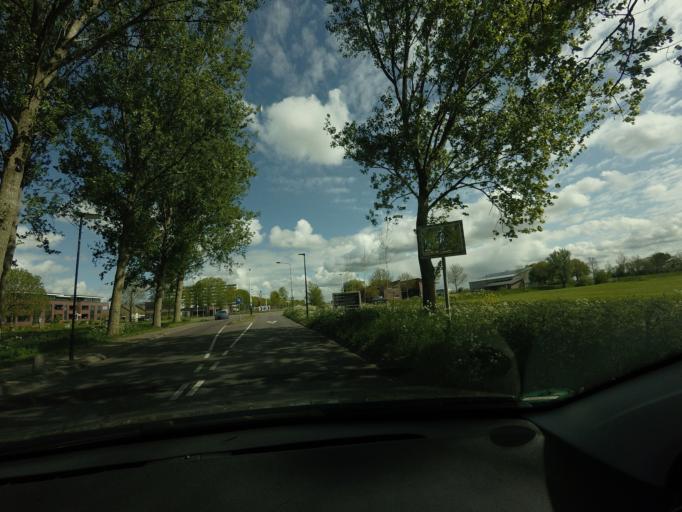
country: NL
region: Friesland
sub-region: Sudwest Fryslan
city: Bolsward
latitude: 53.0594
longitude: 5.5381
